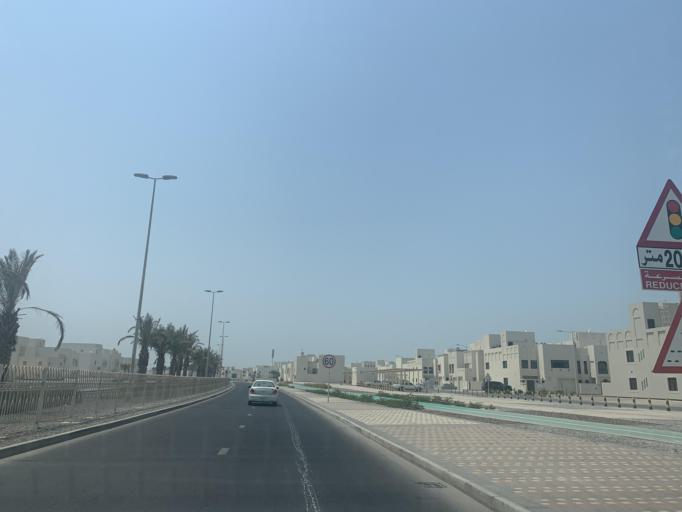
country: BH
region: Muharraq
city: Al Hadd
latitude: 26.2324
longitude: 50.6706
